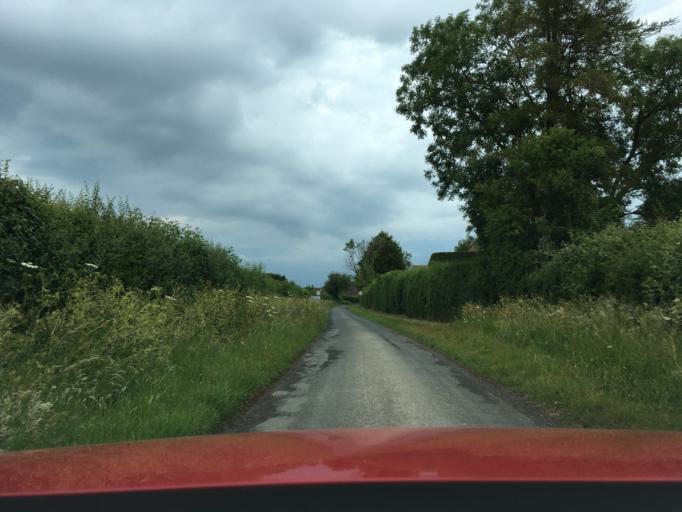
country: GB
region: England
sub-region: Gloucestershire
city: Shurdington
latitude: 51.8091
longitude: -2.0875
